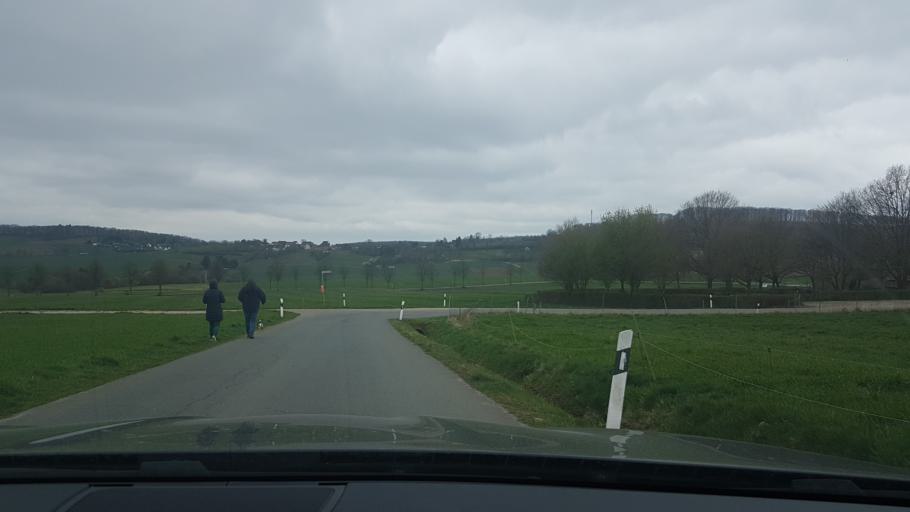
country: DE
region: Lower Saxony
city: Hameln
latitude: 52.1552
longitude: 9.3864
